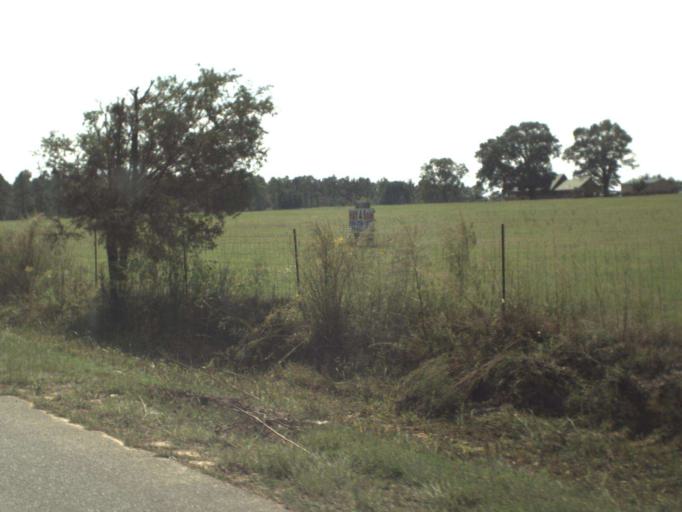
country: US
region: Florida
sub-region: Holmes County
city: Bonifay
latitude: 30.8455
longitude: -85.6668
